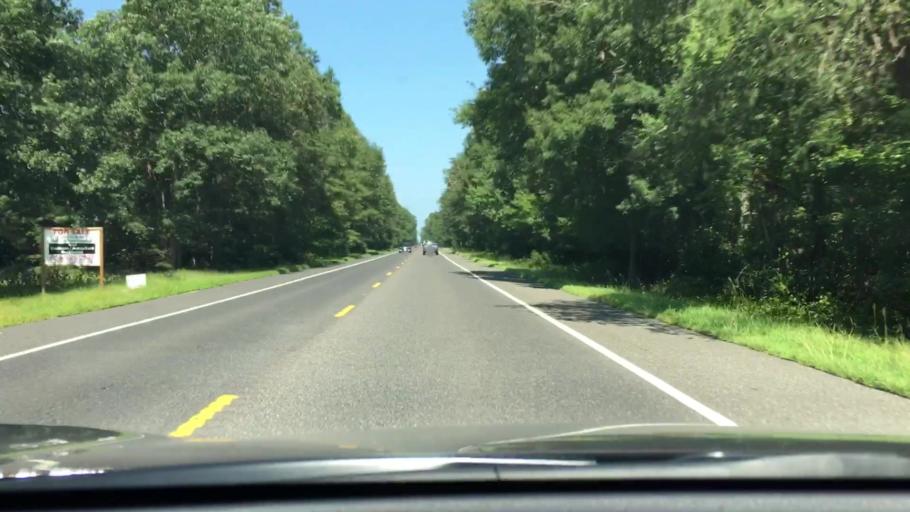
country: US
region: New Jersey
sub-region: Cumberland County
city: Port Norris
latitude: 39.2614
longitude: -74.9327
